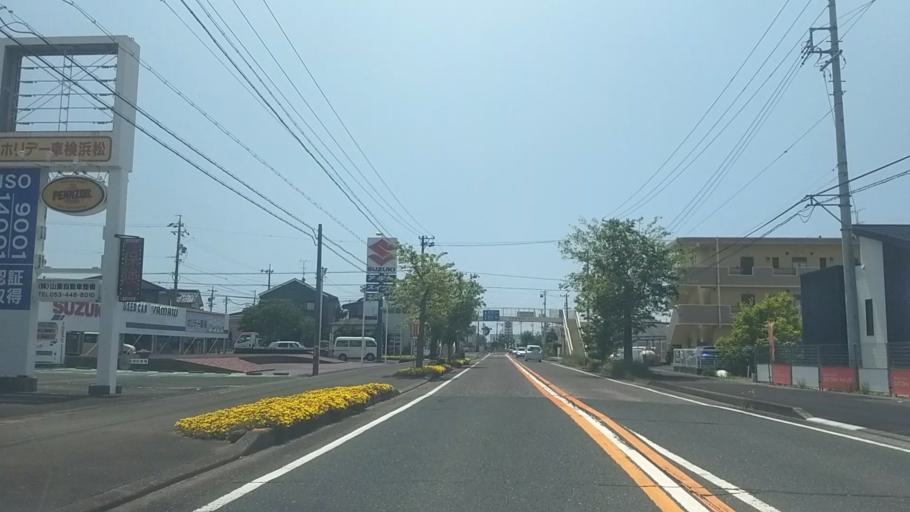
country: JP
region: Shizuoka
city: Hamamatsu
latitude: 34.6852
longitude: 137.6702
